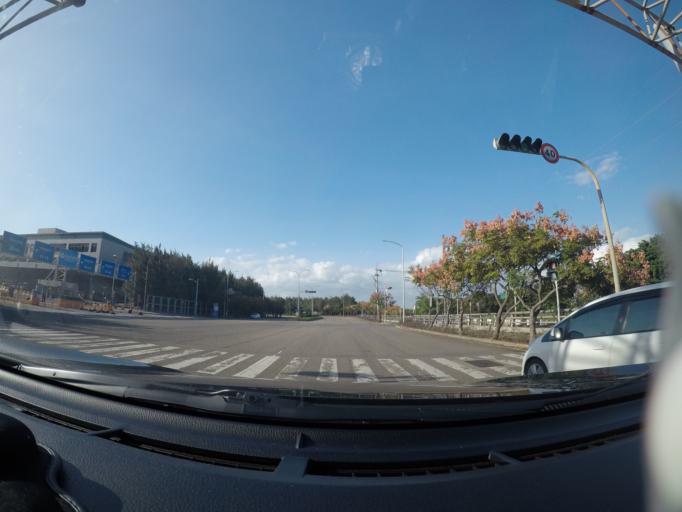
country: TW
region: Taiwan
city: Taoyuan City
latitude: 25.0995
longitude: 121.2550
